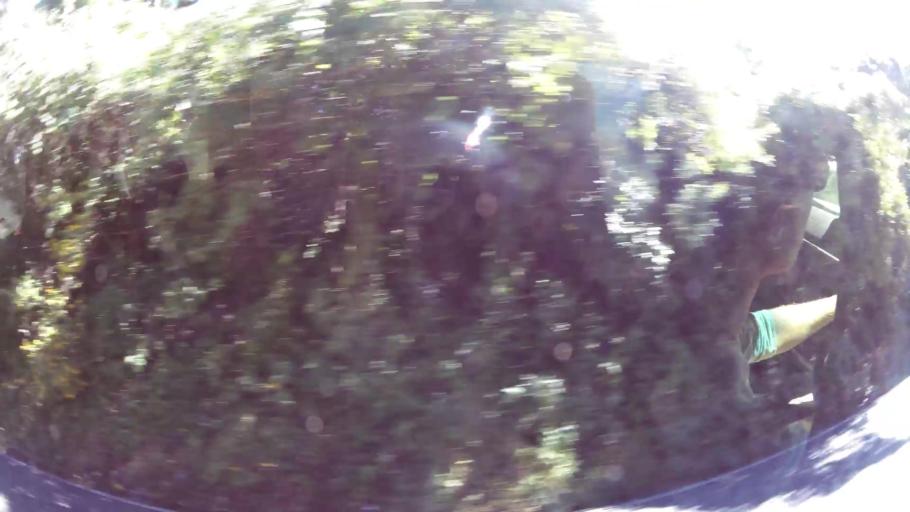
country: GT
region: Solola
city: Solola
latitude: 14.7525
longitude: -91.1705
